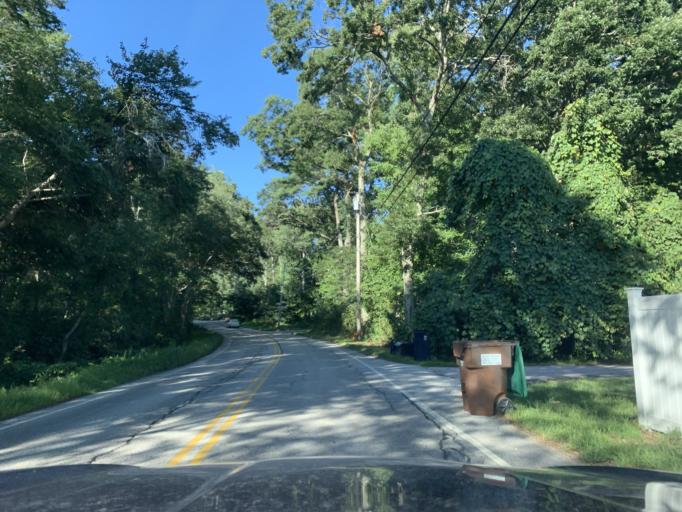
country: US
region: Rhode Island
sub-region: Washington County
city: North Kingstown
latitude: 41.5556
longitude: -71.4969
